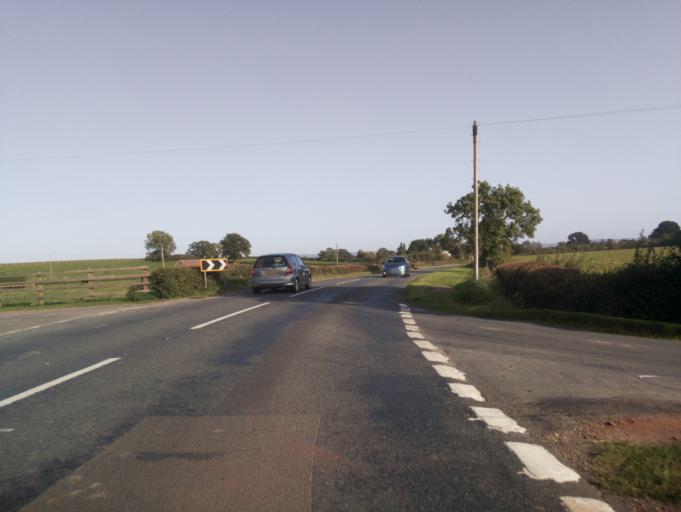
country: GB
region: England
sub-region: Gloucestershire
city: Gloucester
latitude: 51.9603
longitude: -2.2521
